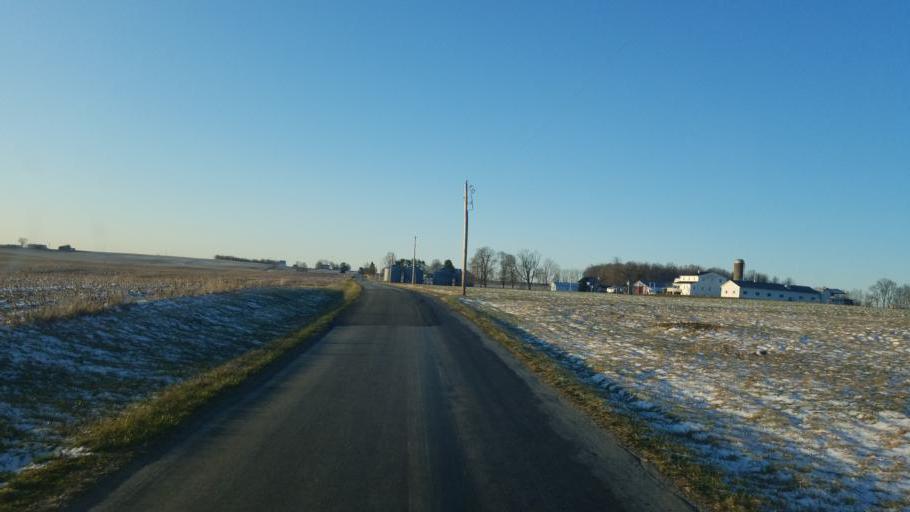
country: US
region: Ohio
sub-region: Highland County
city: Leesburg
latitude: 39.2513
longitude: -83.5014
